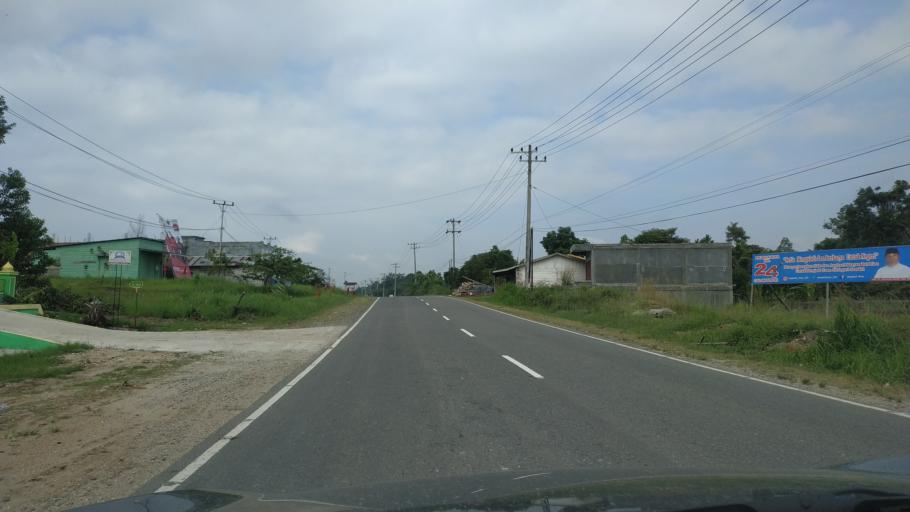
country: ID
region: Riau
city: Rengat
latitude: -0.3940
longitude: 102.4321
